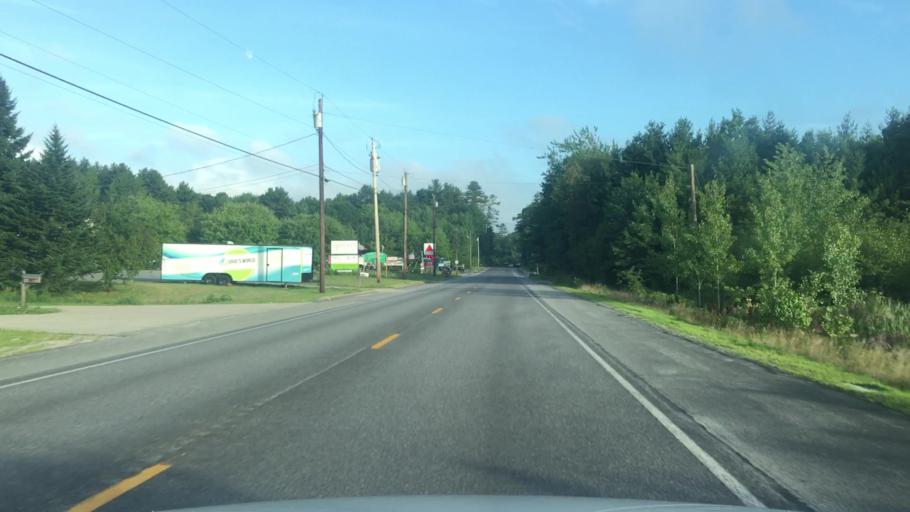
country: US
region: Maine
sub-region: Cumberland County
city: North Windham
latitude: 43.7966
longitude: -70.4009
